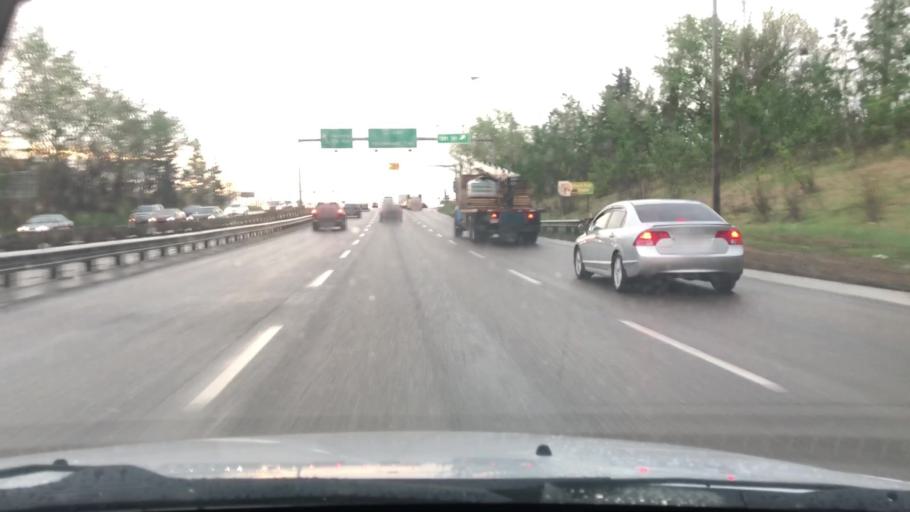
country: CA
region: Alberta
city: Edmonton
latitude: 53.5806
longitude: -113.5298
